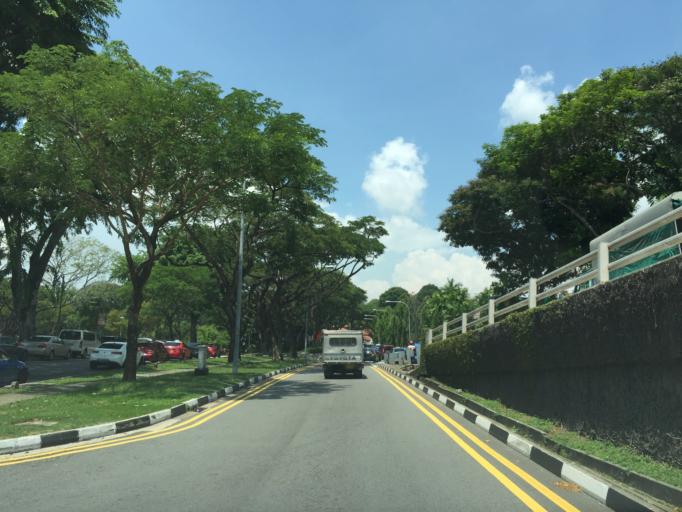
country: SG
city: Singapore
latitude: 1.3127
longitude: 103.8453
